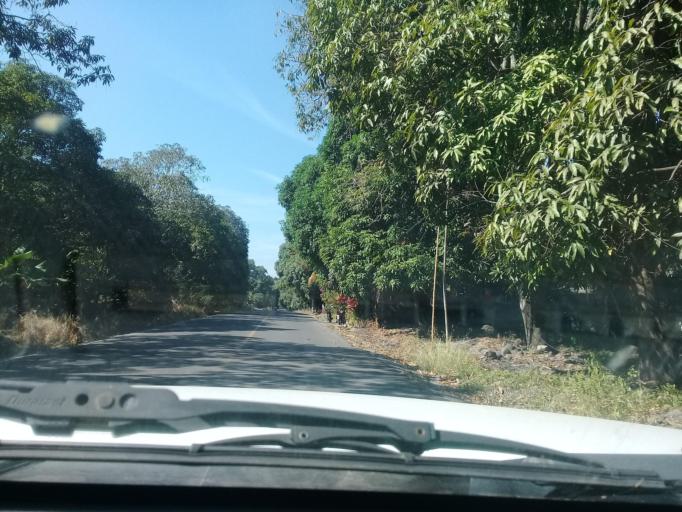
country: MX
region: Veracruz
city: Actopan
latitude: 19.4771
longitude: -96.5690
